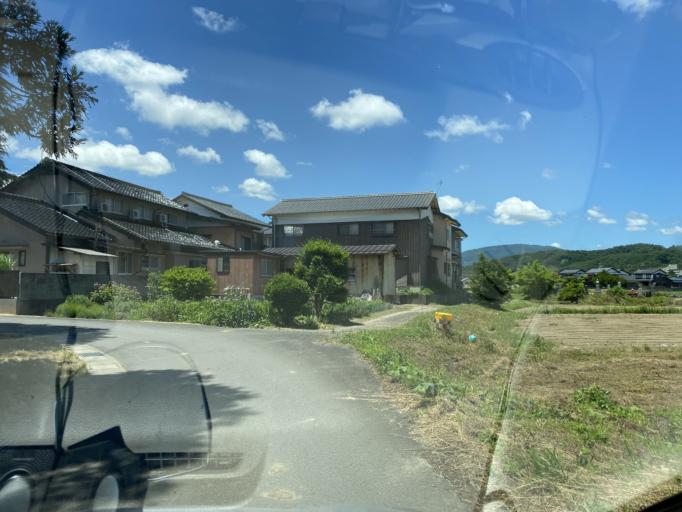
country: JP
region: Hyogo
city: Toyooka
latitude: 35.4923
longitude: 134.8072
